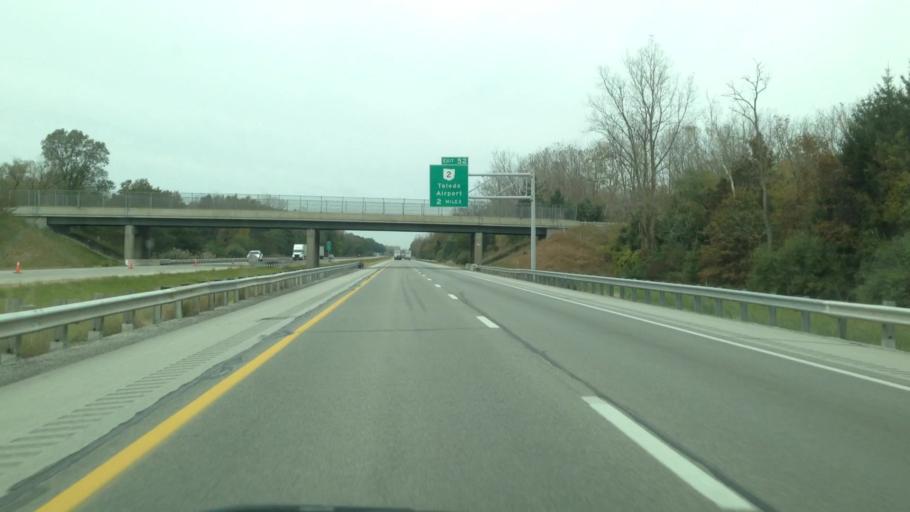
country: US
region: Ohio
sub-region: Lucas County
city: Holland
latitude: 41.5927
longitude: -83.7600
